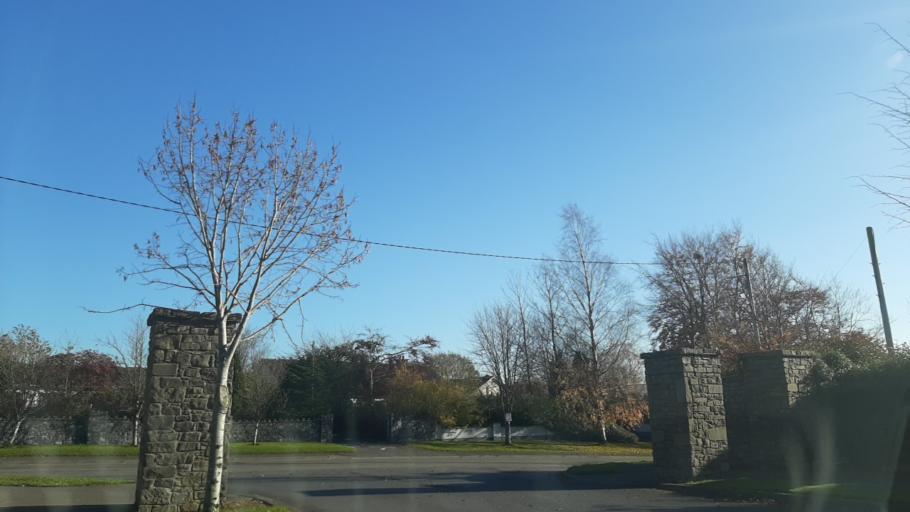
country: IE
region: Leinster
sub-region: Kildare
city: Rathangan
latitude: 53.2199
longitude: -7.0046
